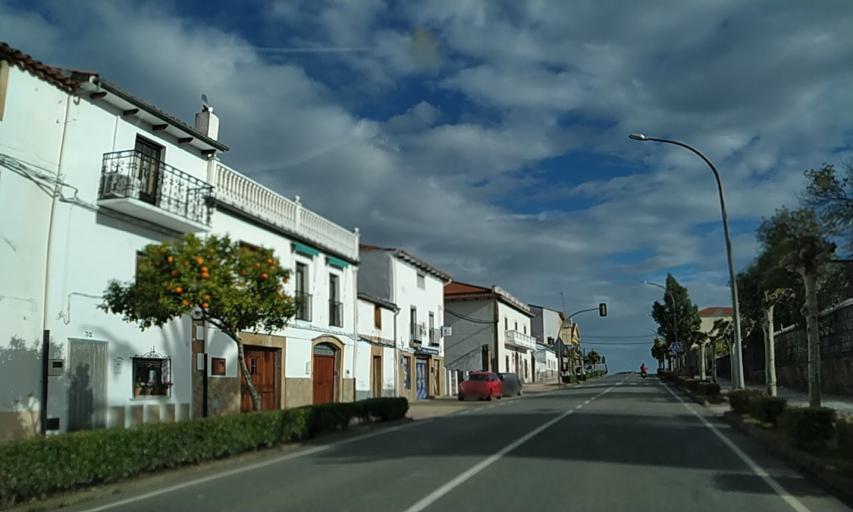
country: ES
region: Extremadura
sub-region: Provincia de Caceres
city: Perales del Puerto
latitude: 40.1557
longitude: -6.6815
